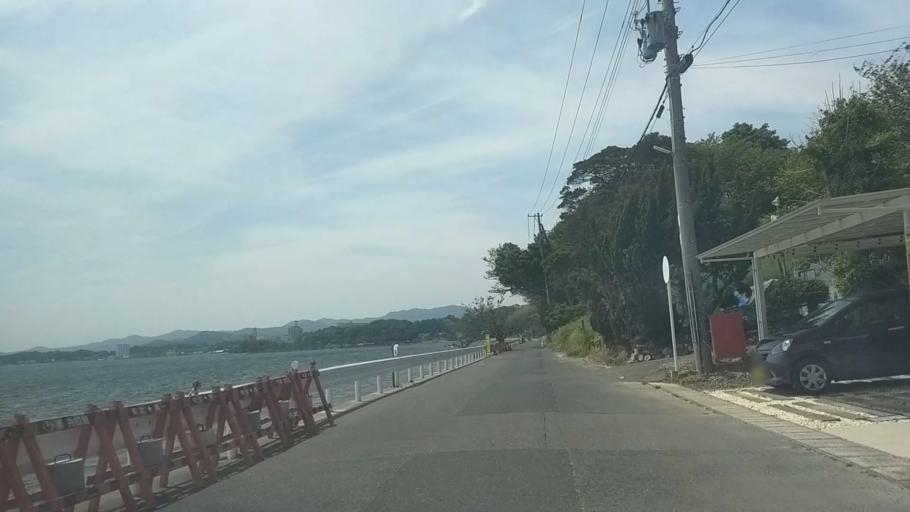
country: JP
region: Shizuoka
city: Kosai-shi
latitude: 34.7843
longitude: 137.5934
